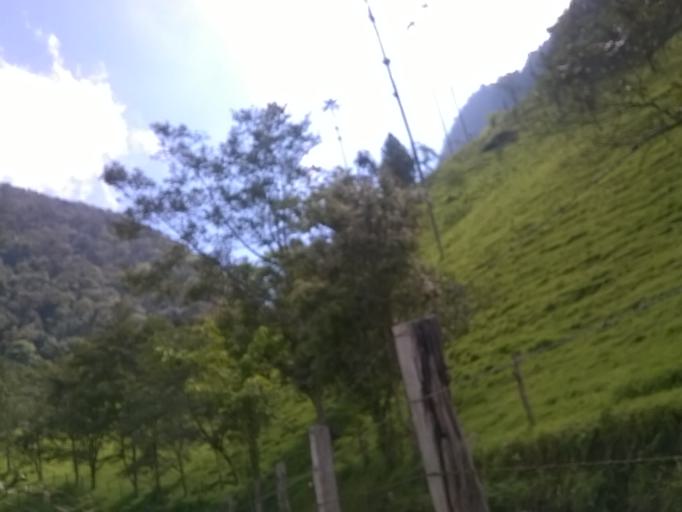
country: CO
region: Quindio
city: Salento
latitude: 4.6307
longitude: -75.4714
